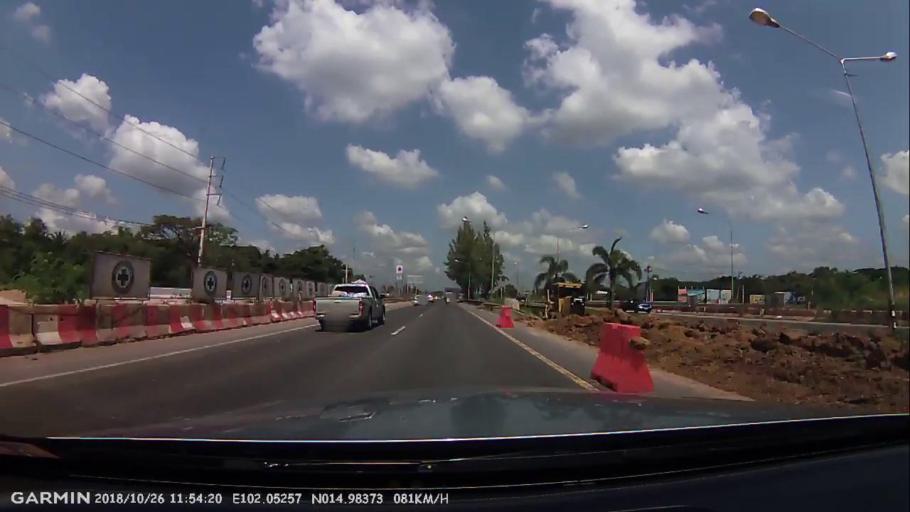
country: TH
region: Nakhon Ratchasima
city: Nakhon Ratchasima
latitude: 14.9840
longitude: 102.0526
